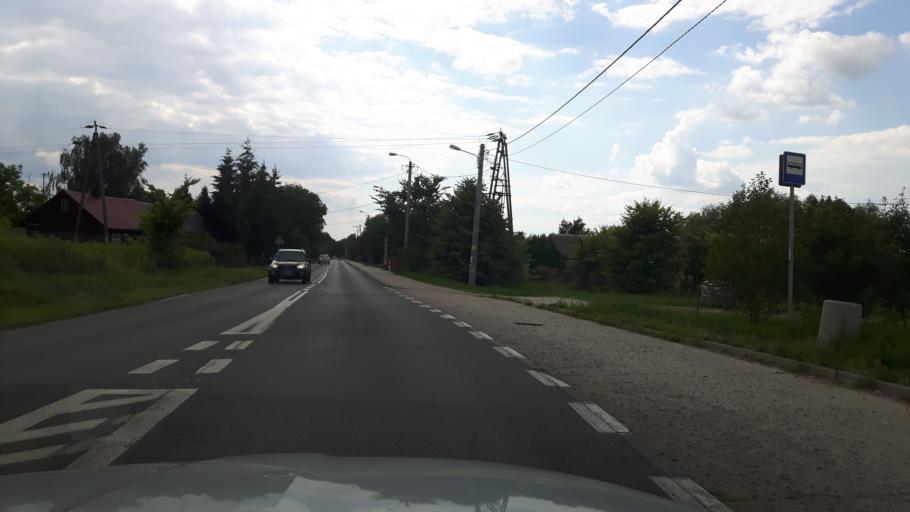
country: PL
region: Masovian Voivodeship
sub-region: Powiat wolominski
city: Ostrowek
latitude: 52.3809
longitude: 21.3996
